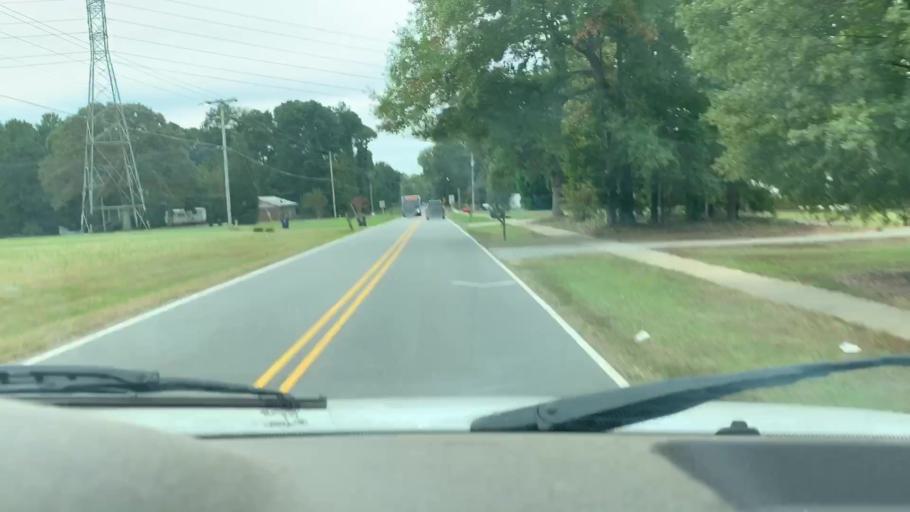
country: US
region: North Carolina
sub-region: Mecklenburg County
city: Cornelius
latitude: 35.4629
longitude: -80.8674
